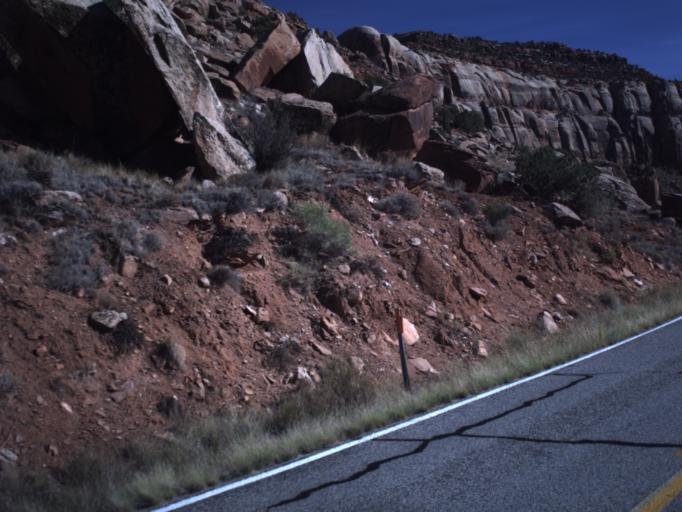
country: US
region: Utah
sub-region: San Juan County
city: Monticello
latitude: 38.0483
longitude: -109.5531
